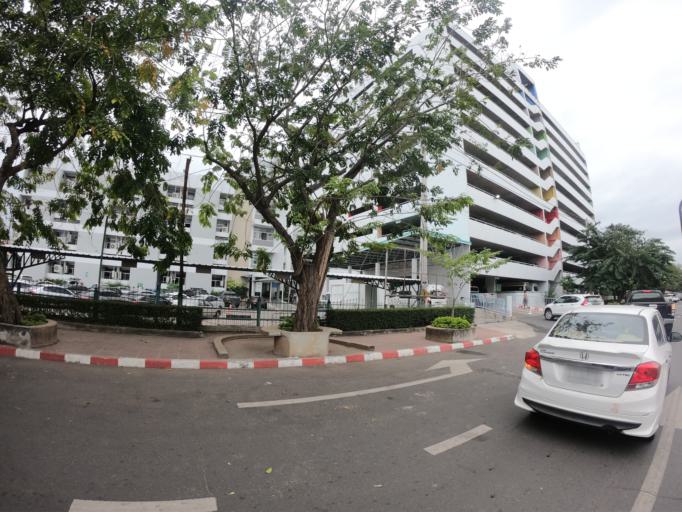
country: TH
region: Roi Et
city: Roi Et
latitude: 16.0497
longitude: 103.6536
